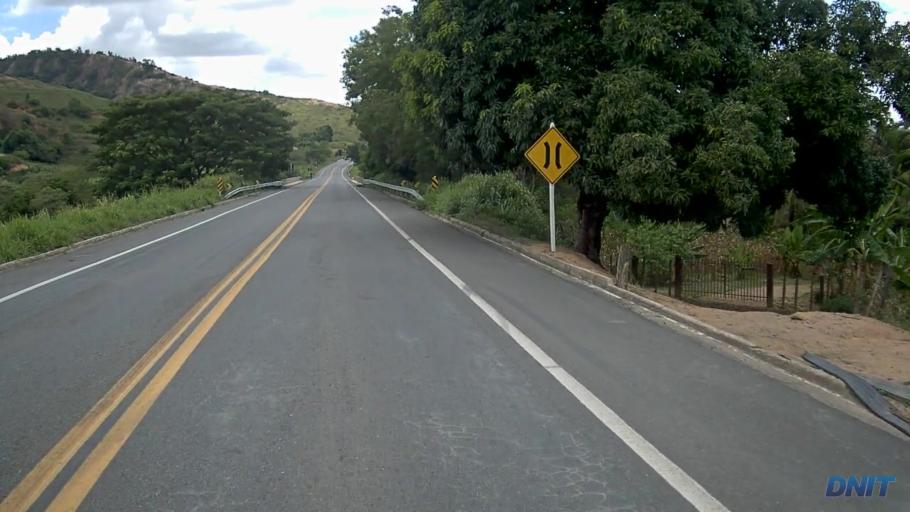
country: BR
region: Minas Gerais
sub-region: Governador Valadares
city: Governador Valadares
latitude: -18.9468
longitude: -42.0676
